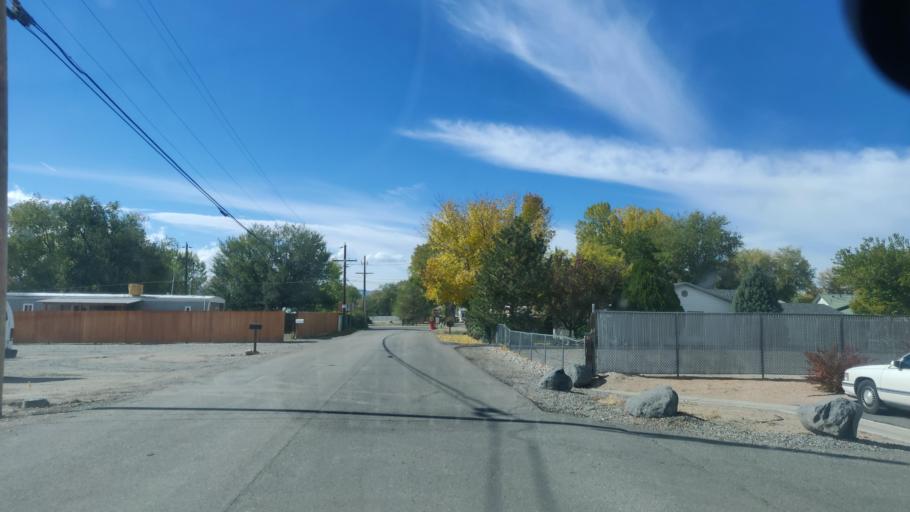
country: US
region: Colorado
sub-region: Mesa County
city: Fruitvale
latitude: 39.0792
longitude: -108.5138
